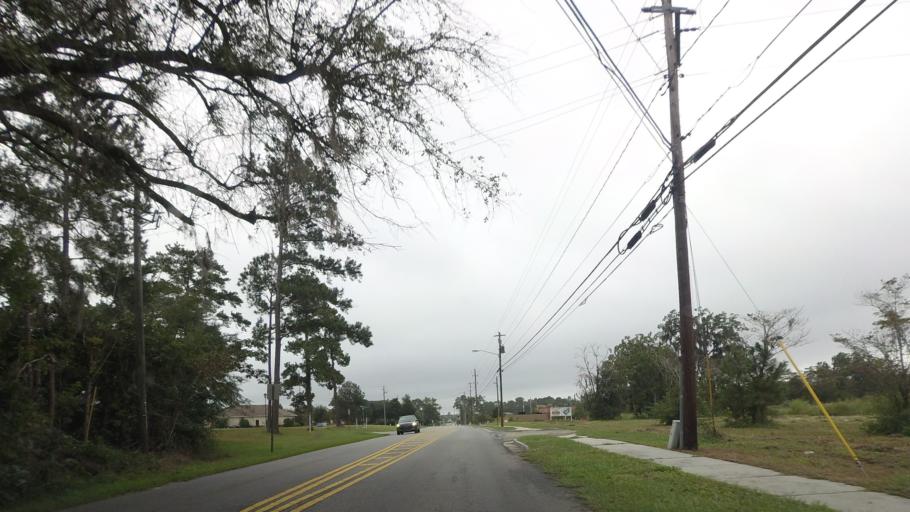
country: US
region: Georgia
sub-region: Lowndes County
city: Remerton
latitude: 30.8814
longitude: -83.2979
